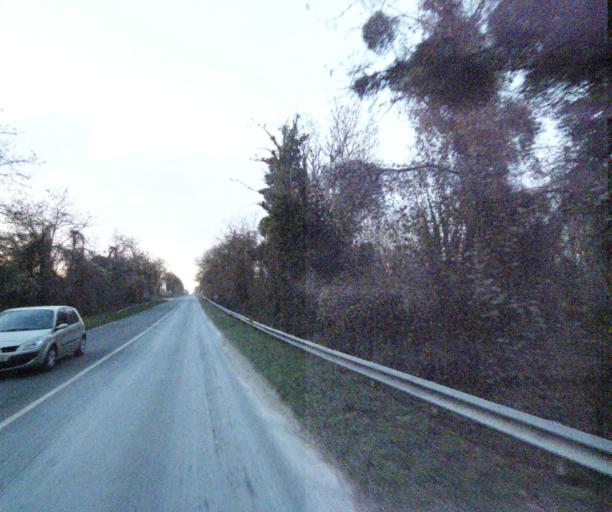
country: FR
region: Poitou-Charentes
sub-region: Departement de la Charente-Maritime
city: Saint-Porchaire
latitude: 45.8140
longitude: -0.7705
